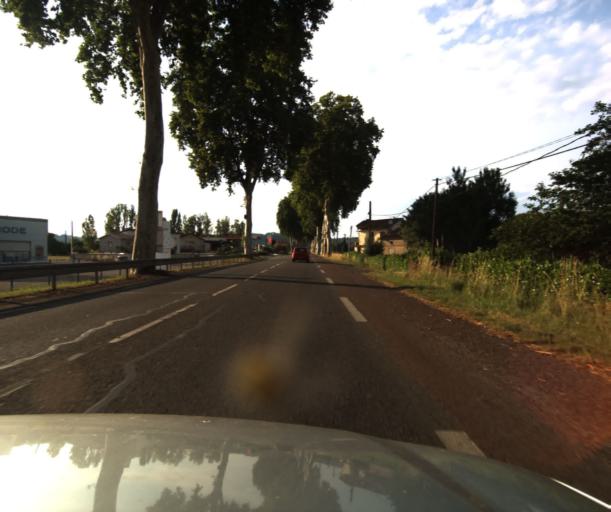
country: FR
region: Midi-Pyrenees
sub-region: Departement du Tarn-et-Garonne
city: Moissac
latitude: 44.0900
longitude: 1.0878
